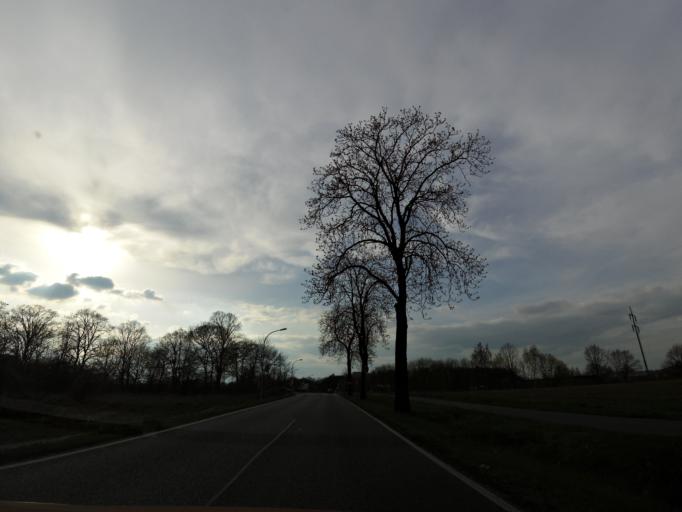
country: DE
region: Brandenburg
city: Grossbeeren
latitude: 52.3422
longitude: 13.3582
